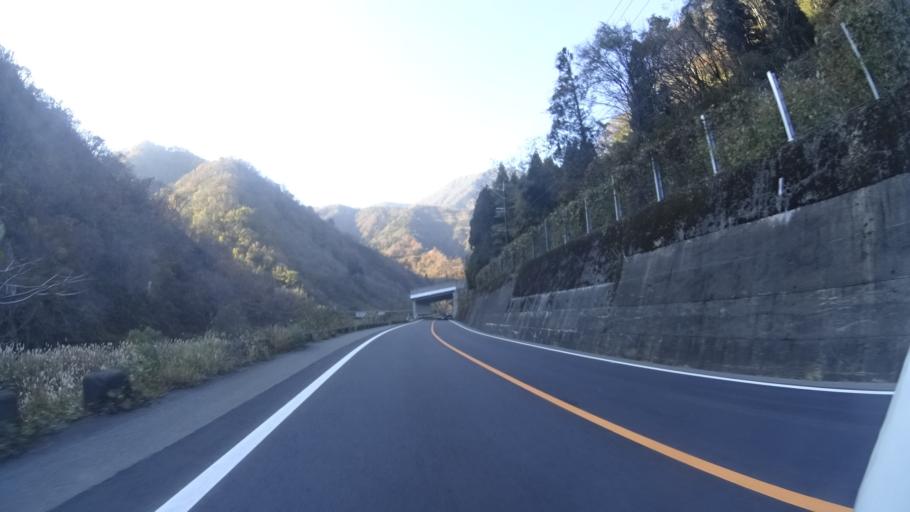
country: JP
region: Fukui
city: Ono
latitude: 35.9113
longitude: 136.6295
